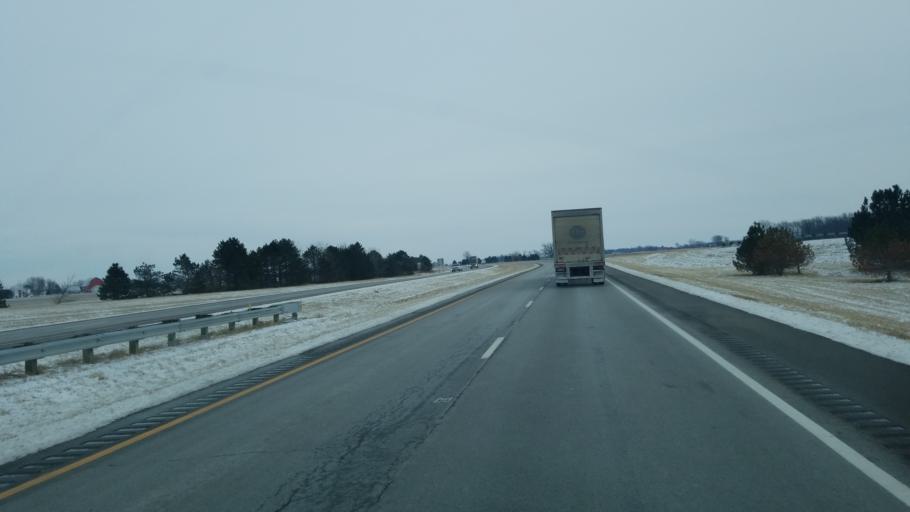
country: US
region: Ohio
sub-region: Wyandot County
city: Carey
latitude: 40.9693
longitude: -83.4840
